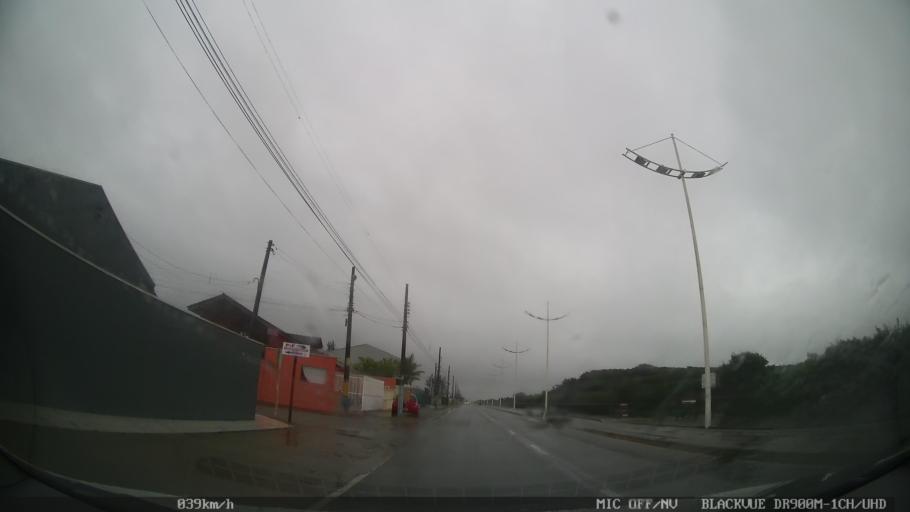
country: BR
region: Santa Catarina
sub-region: Navegantes
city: Navegantes
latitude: -26.8856
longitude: -48.6419
